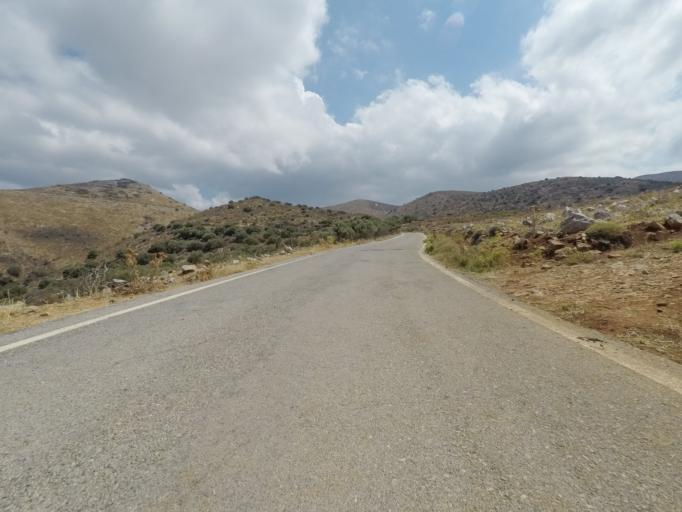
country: GR
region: Crete
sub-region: Nomos Lasithiou
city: Elounda
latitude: 35.3166
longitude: 25.6761
